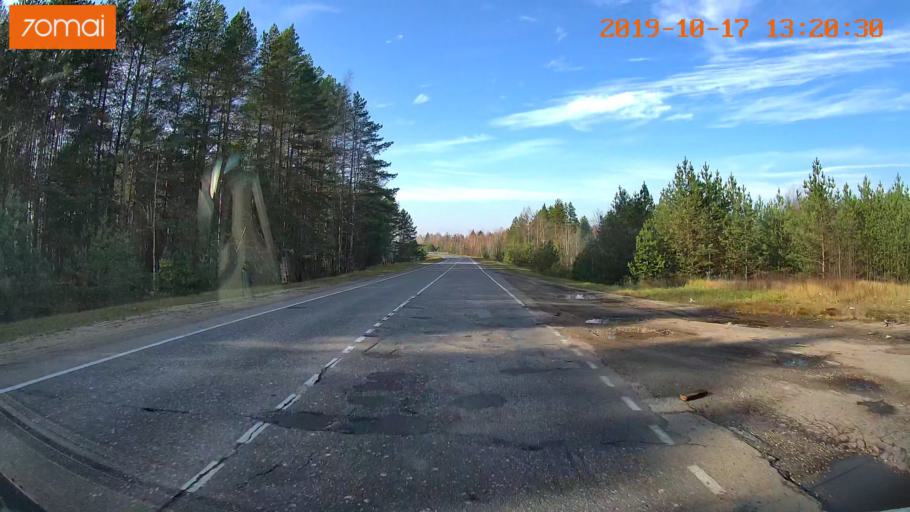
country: RU
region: Rjazan
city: Gus'-Zheleznyy
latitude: 55.0765
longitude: 41.0489
